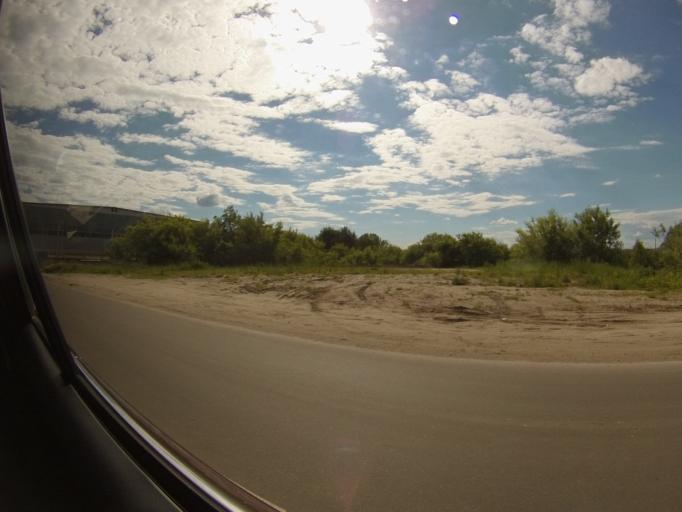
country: RU
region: Orjol
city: Mtsensk
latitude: 53.2929
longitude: 36.5870
